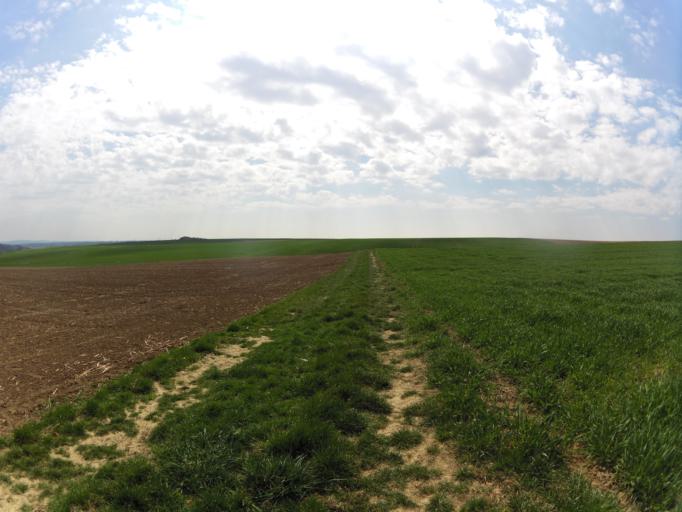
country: DE
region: Bavaria
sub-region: Regierungsbezirk Unterfranken
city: Winterhausen
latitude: 49.6875
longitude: 10.0057
